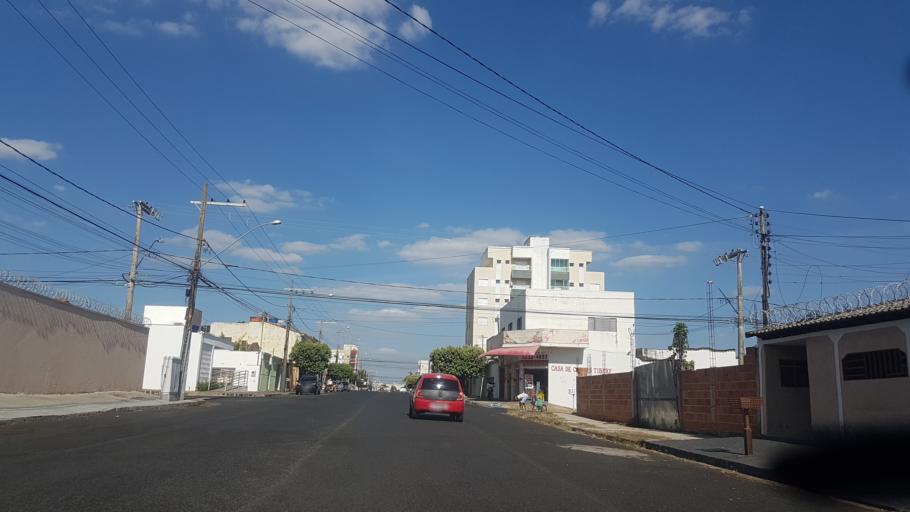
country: BR
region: Minas Gerais
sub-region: Uberlandia
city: Uberlandia
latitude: -18.9032
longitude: -48.2562
